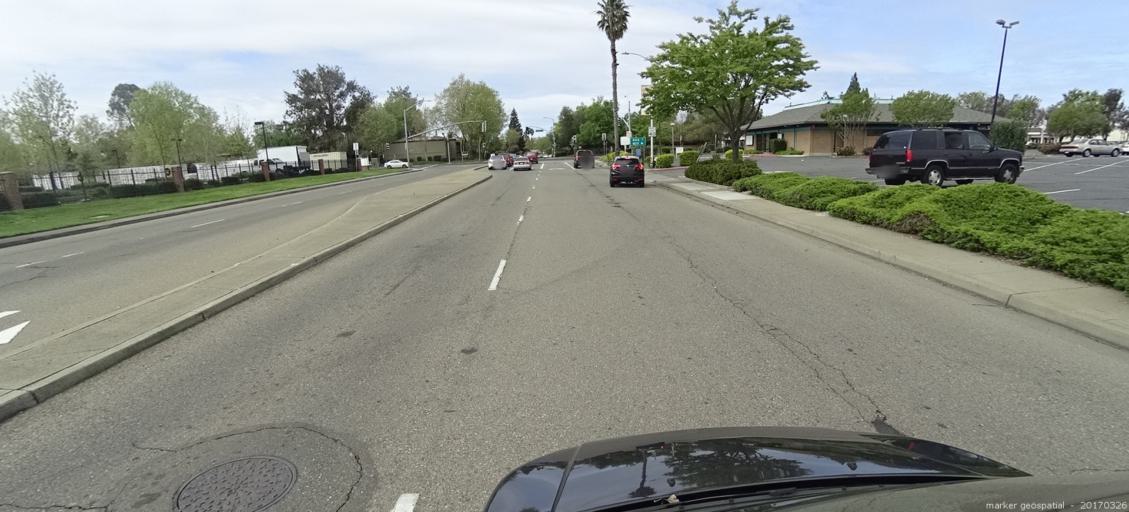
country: US
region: California
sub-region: Sacramento County
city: Florin
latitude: 38.4707
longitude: -121.4259
